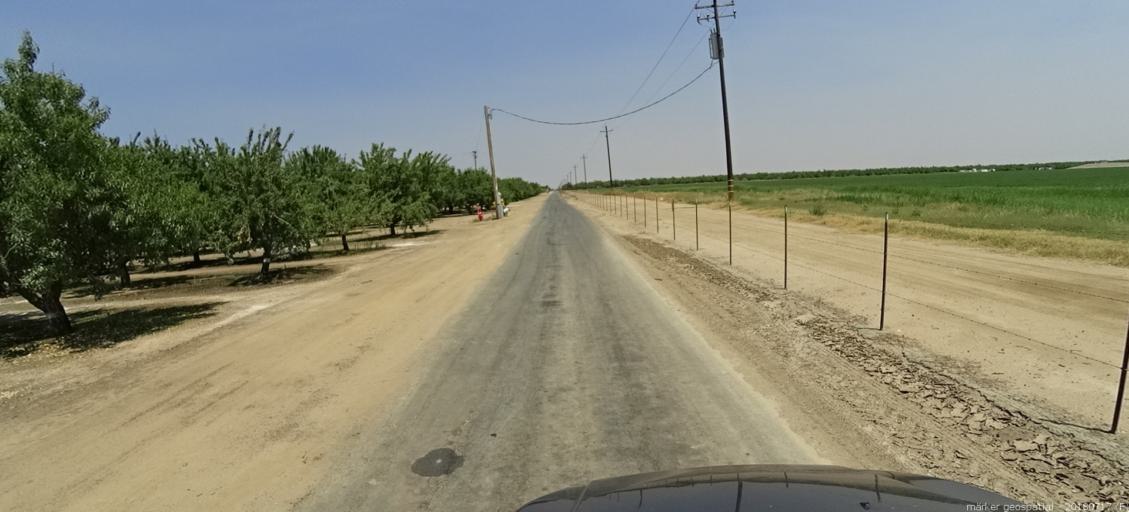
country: US
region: California
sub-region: Madera County
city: Fairmead
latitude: 37.1043
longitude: -120.1659
